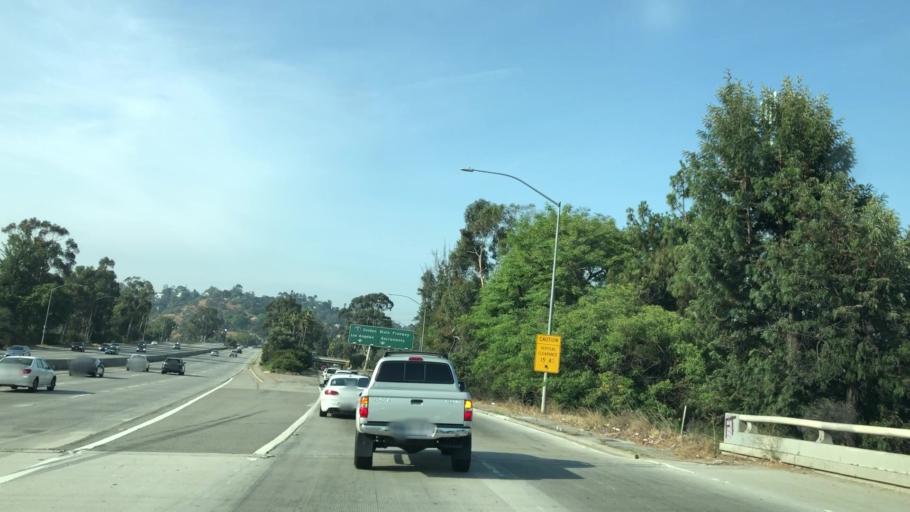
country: US
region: California
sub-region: Los Angeles County
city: Silver Lake
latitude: 34.1081
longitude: -118.2499
